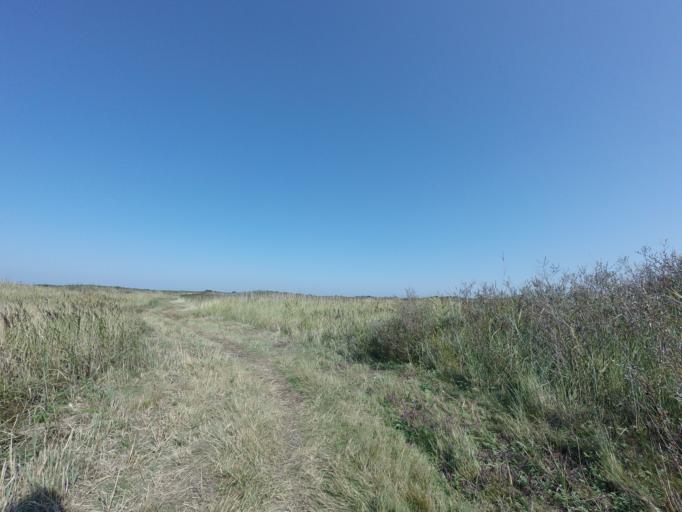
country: NL
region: Friesland
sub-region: Gemeente Schiermonnikoog
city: Schiermonnikoog
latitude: 53.4933
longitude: 6.2434
